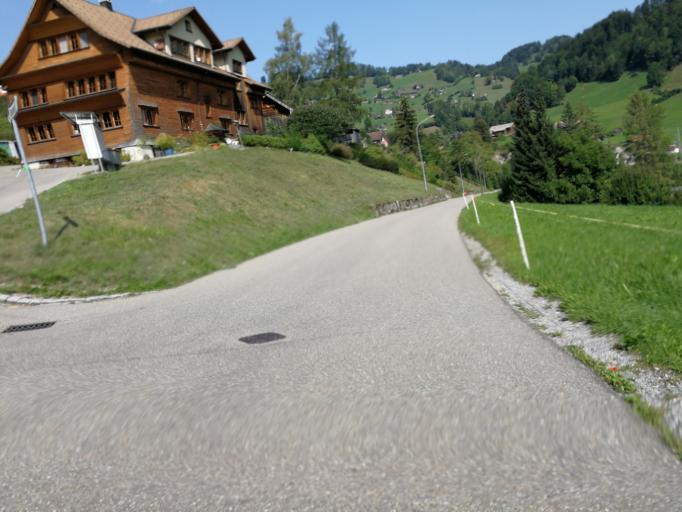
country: CH
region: Saint Gallen
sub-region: Wahlkreis Toggenburg
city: Krummenau
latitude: 47.2468
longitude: 9.1658
